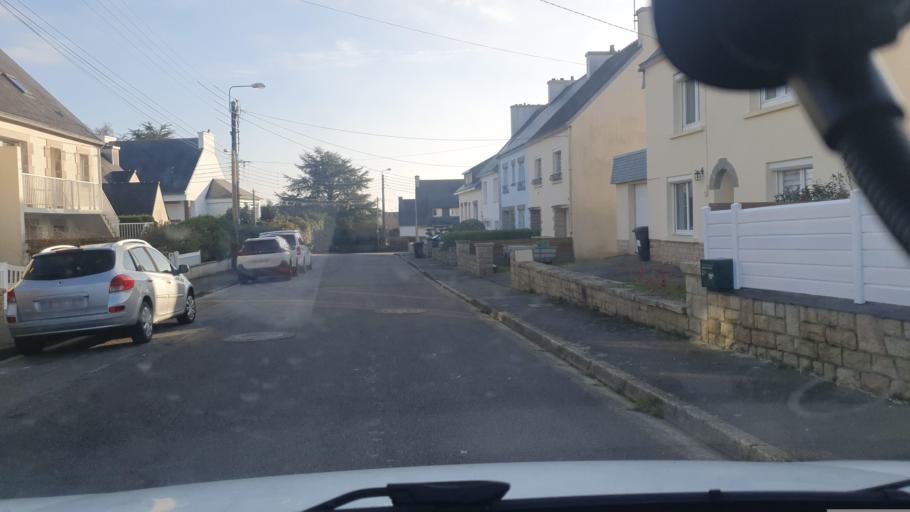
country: FR
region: Brittany
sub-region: Departement du Finistere
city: Briec
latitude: 48.1010
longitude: -4.0037
